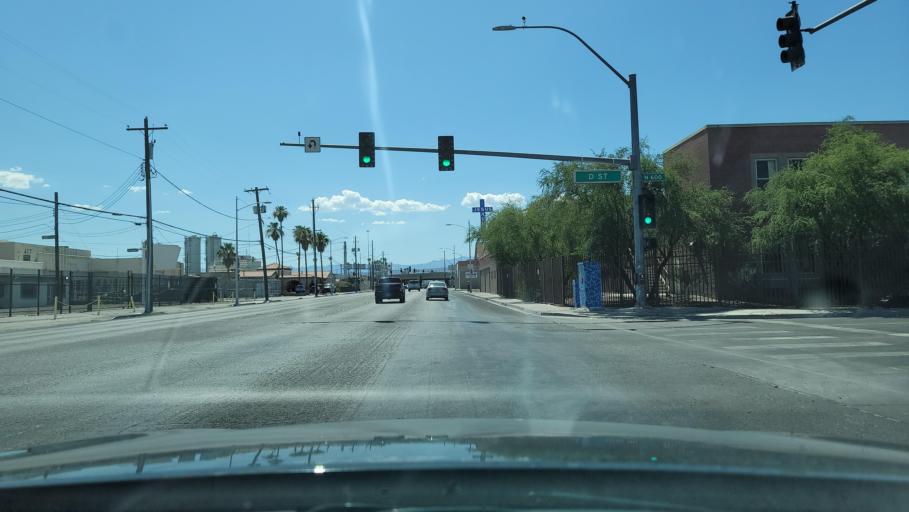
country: US
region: Nevada
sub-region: Clark County
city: Las Vegas
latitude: 36.1774
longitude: -115.1466
